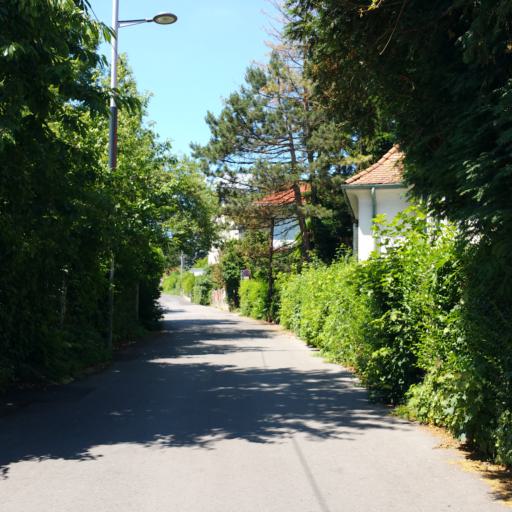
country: AT
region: Vienna
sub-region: Wien Stadt
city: Vienna
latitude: 48.2160
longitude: 16.2969
